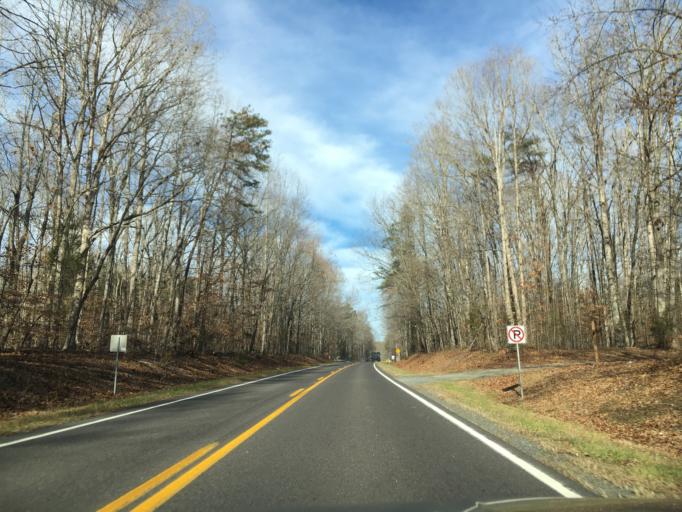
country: US
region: Virginia
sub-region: Louisa County
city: Louisa
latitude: 38.1457
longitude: -77.9258
